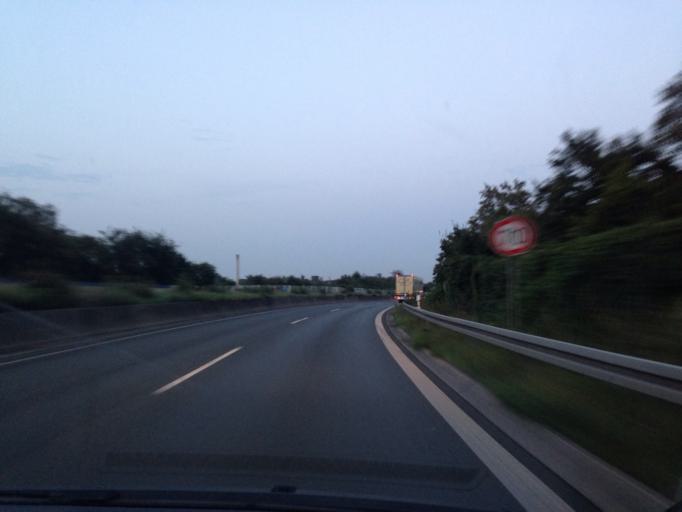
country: DE
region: North Rhine-Westphalia
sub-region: Regierungsbezirk Munster
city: Muenster
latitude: 51.9352
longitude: 7.6046
